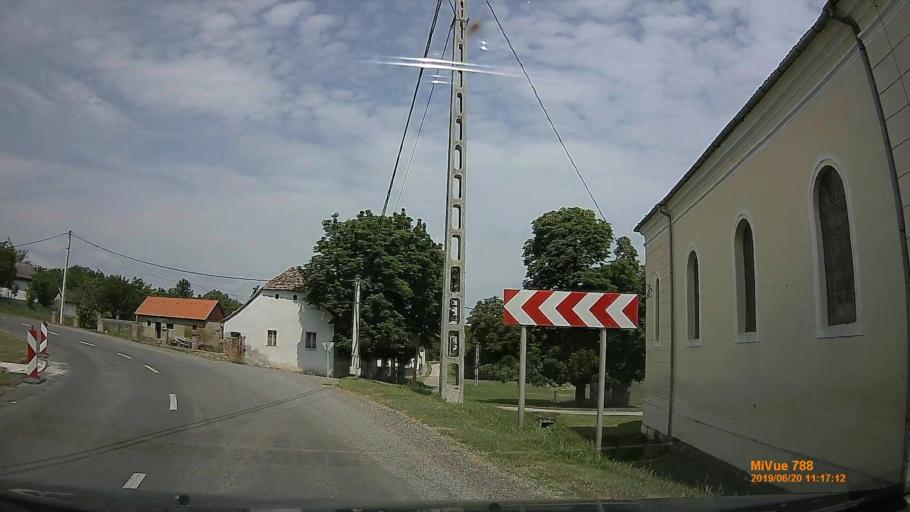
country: HU
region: Baranya
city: Pecsvarad
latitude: 46.1571
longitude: 18.4728
